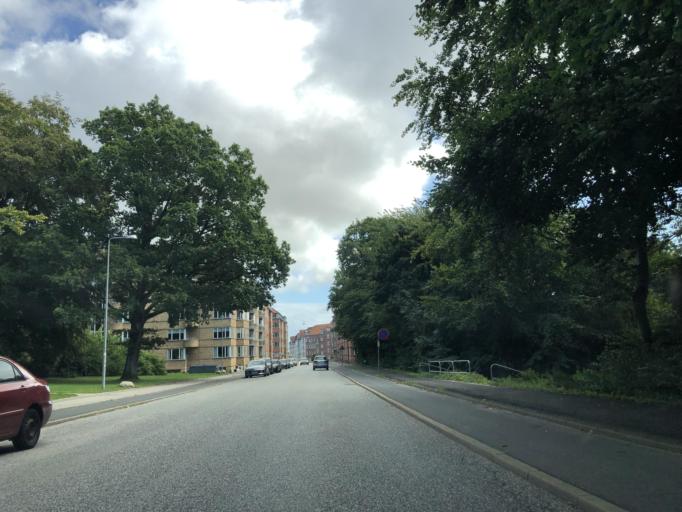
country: DK
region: Central Jutland
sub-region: Randers Kommune
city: Randers
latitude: 56.4658
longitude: 10.0245
